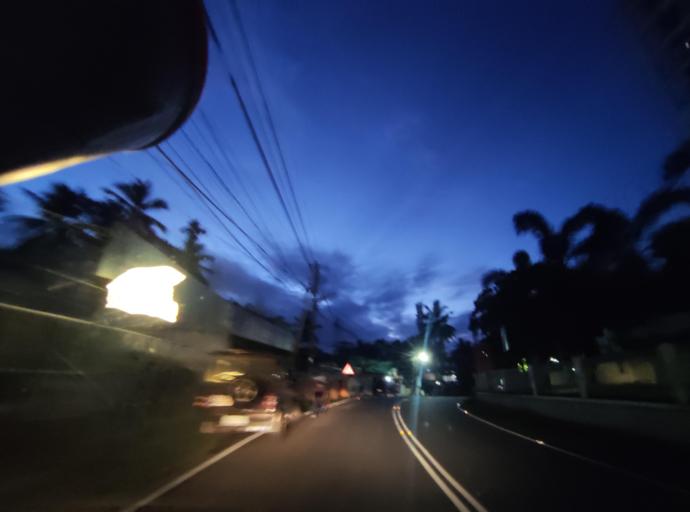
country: IN
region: Kerala
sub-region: Thiruvananthapuram
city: Thiruvananthapuram
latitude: 8.5424
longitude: 76.9610
